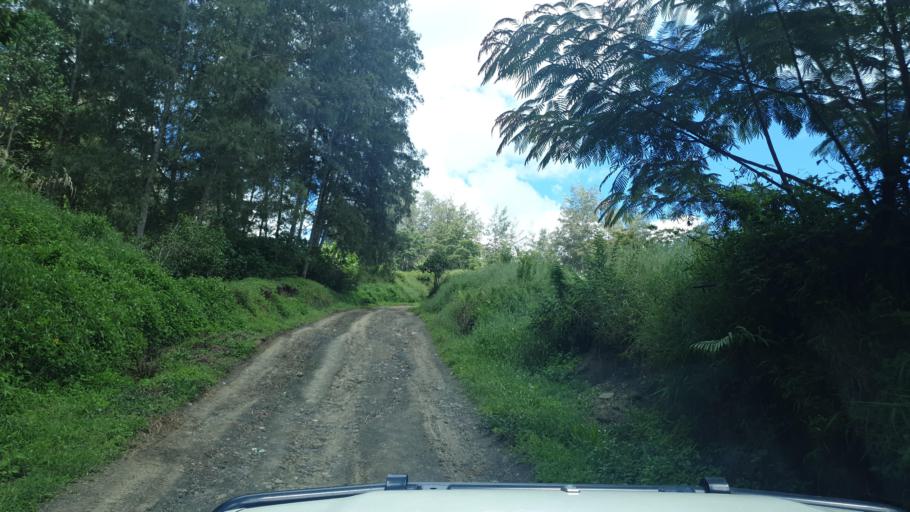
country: PG
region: Chimbu
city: Kundiawa
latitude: -6.2589
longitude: 145.1379
